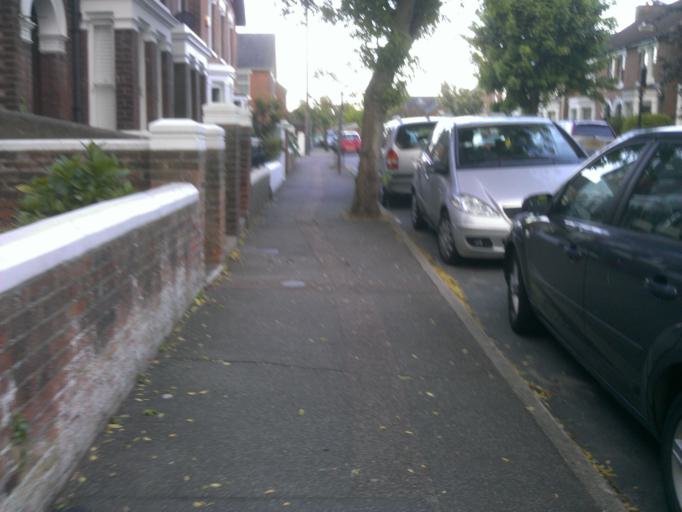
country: GB
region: England
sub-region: Essex
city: Colchester
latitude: 51.8828
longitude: 0.8882
